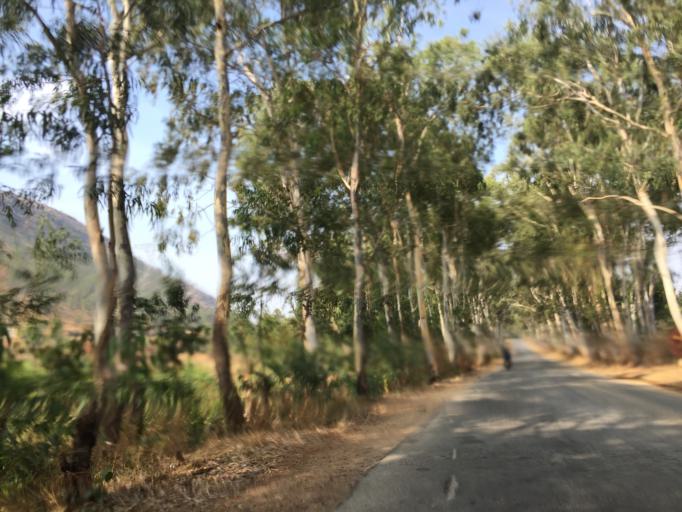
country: IN
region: Karnataka
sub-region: Chikkaballapur
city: Chik Ballapur
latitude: 13.3469
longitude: 77.6751
